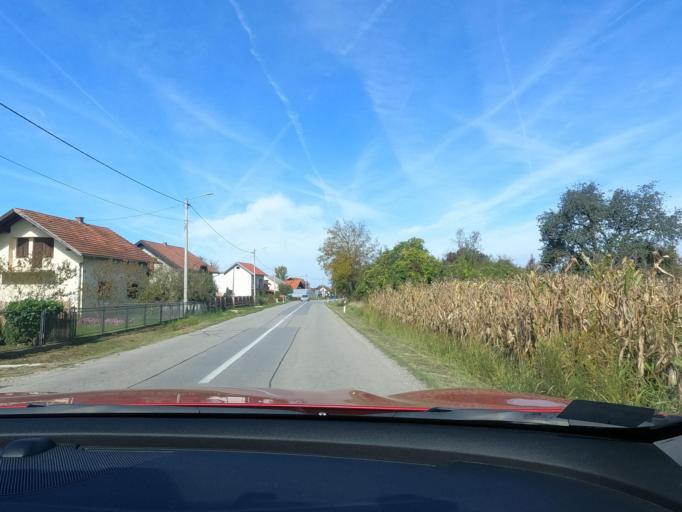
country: HR
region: Sisacko-Moslavacka
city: Petrinja
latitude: 45.4137
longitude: 16.2948
